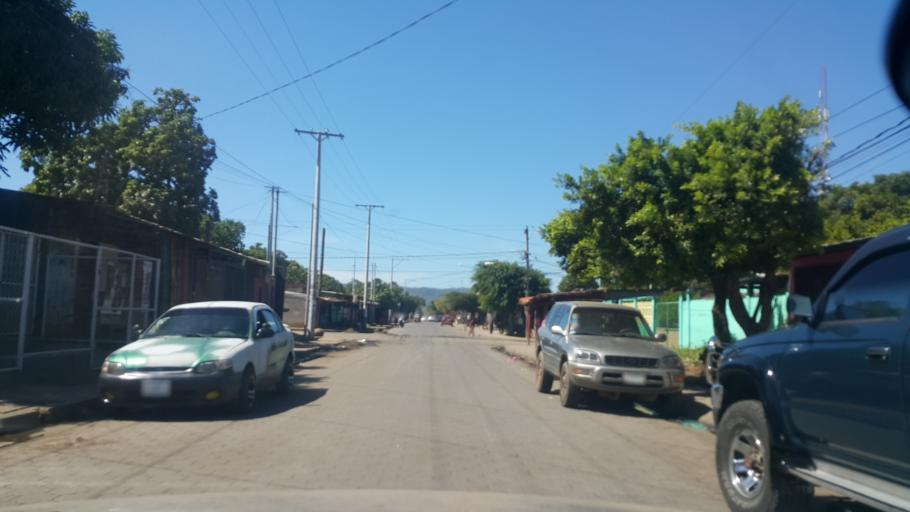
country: NI
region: Managua
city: Ciudad Sandino
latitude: 12.1477
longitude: -86.3451
